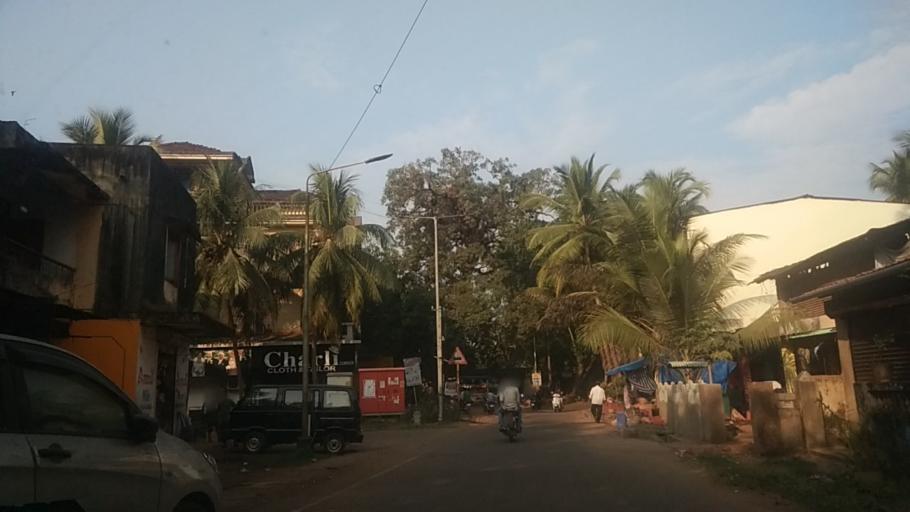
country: IN
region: Goa
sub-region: South Goa
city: Madgaon
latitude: 15.2650
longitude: 73.9578
